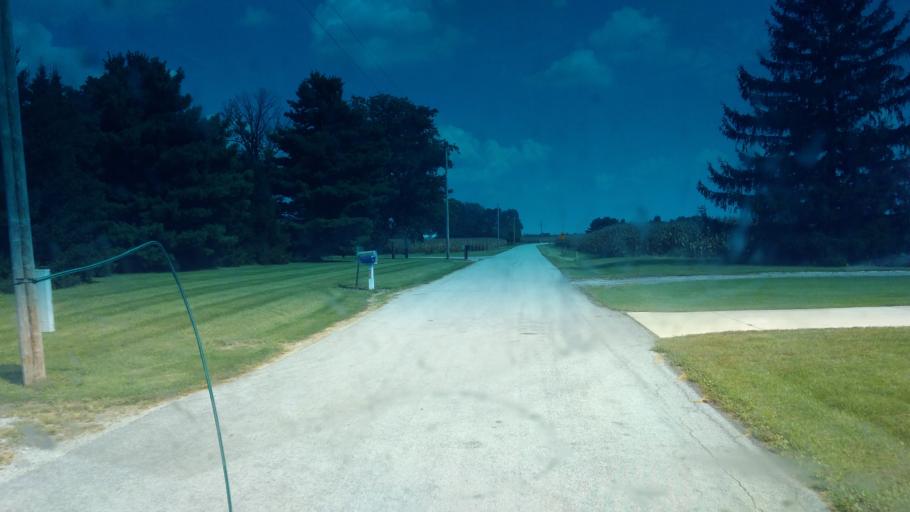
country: US
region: Ohio
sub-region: Hardin County
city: Kenton
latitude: 40.6610
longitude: -83.6963
